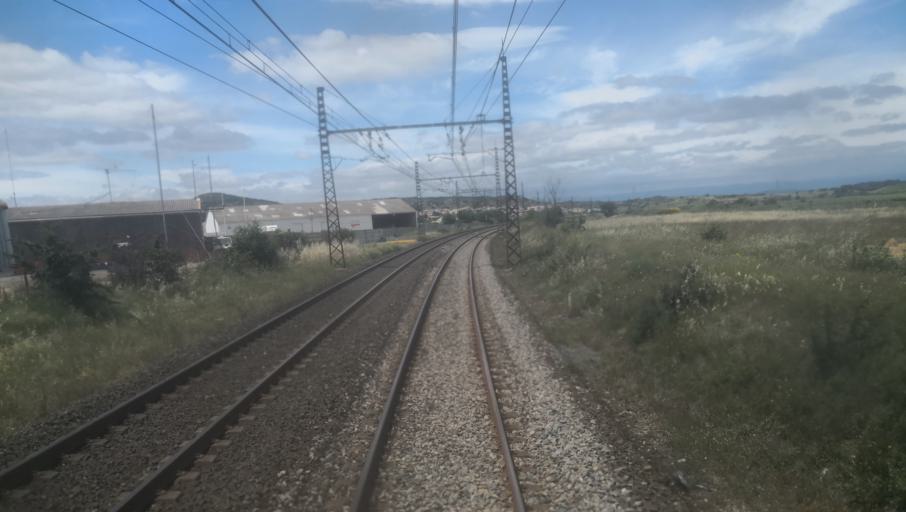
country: FR
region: Languedoc-Roussillon
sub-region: Departement de l'Aude
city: Marcorignan
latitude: 43.1848
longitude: 2.9416
